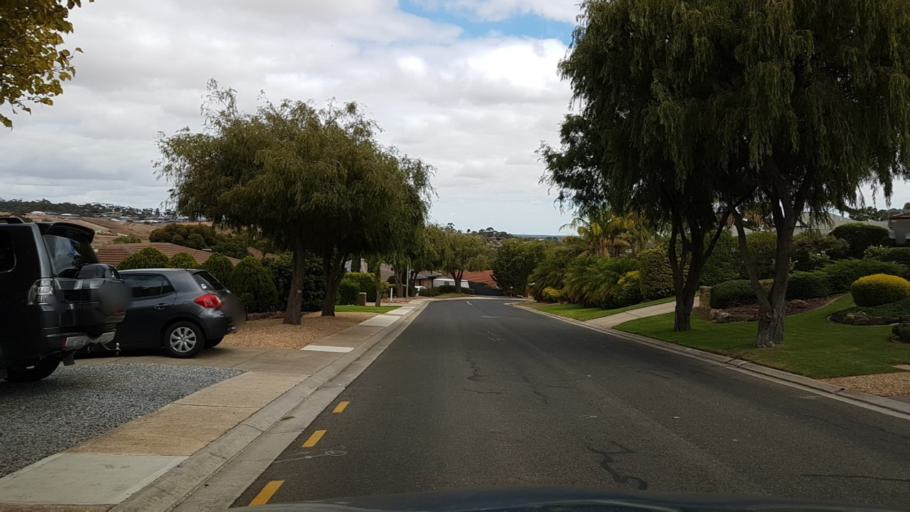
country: AU
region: South Australia
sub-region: Gawler
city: Gawler
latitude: -34.6058
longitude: 138.7614
